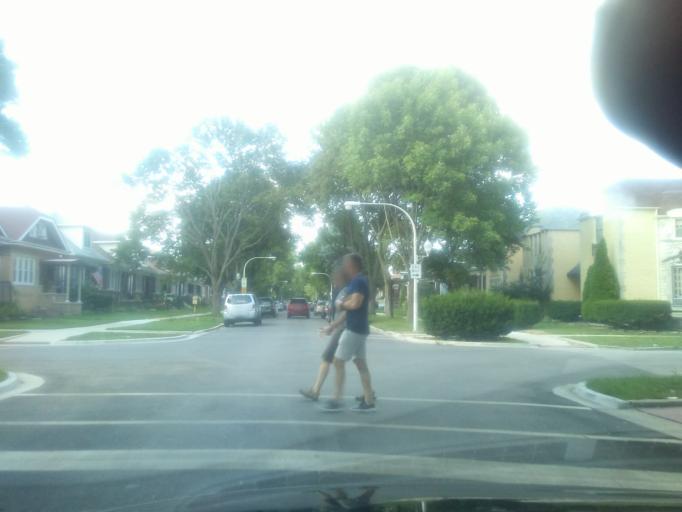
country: US
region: Illinois
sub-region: Cook County
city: Lincolnwood
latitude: 41.9699
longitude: -87.7330
